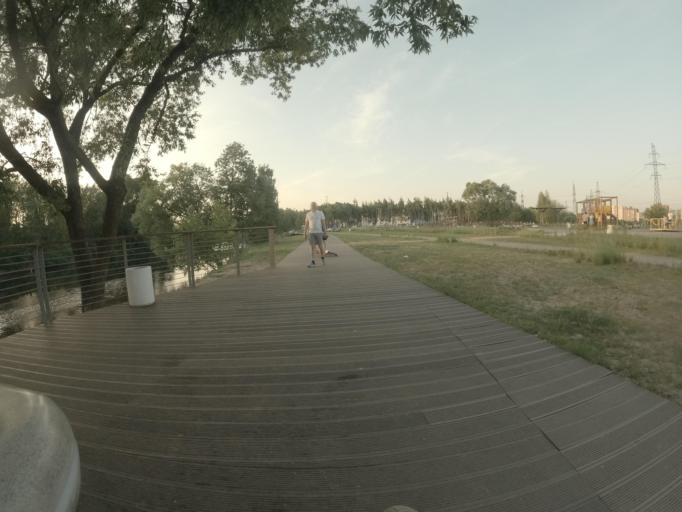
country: RU
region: St.-Petersburg
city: Krasnogvargeisky
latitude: 59.9428
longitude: 30.4558
